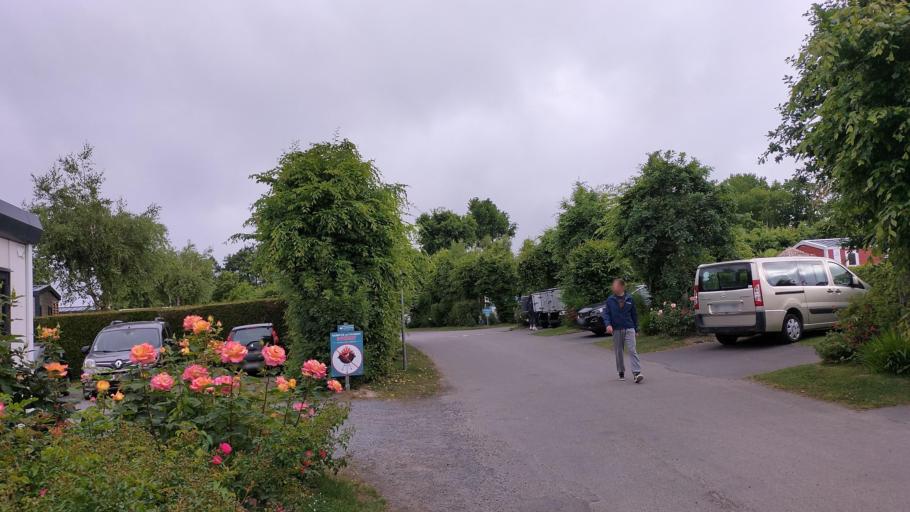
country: FR
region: Brittany
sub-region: Departement d'Ille-et-Vilaine
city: Saint-Jouan-des-Guerets
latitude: 48.6102
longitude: -1.9871
